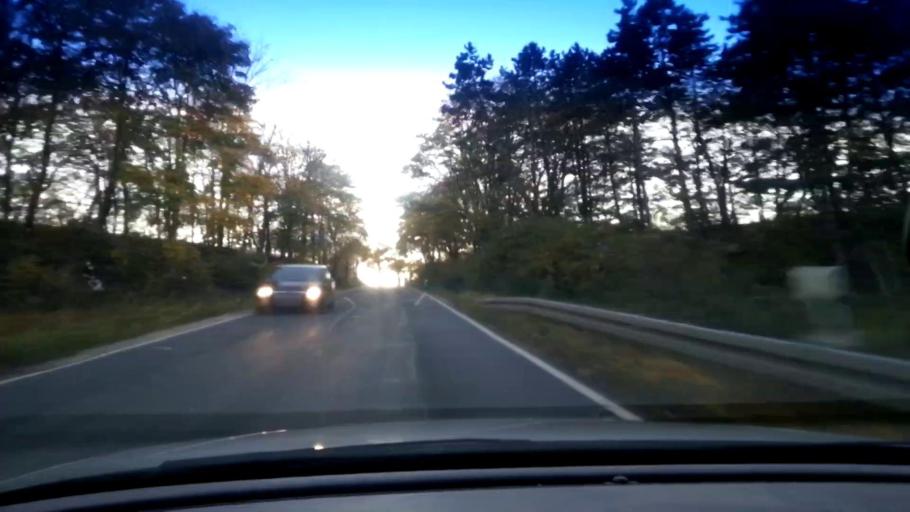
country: DE
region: Bavaria
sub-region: Upper Franconia
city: Heiligenstadt
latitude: 49.8733
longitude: 11.1088
